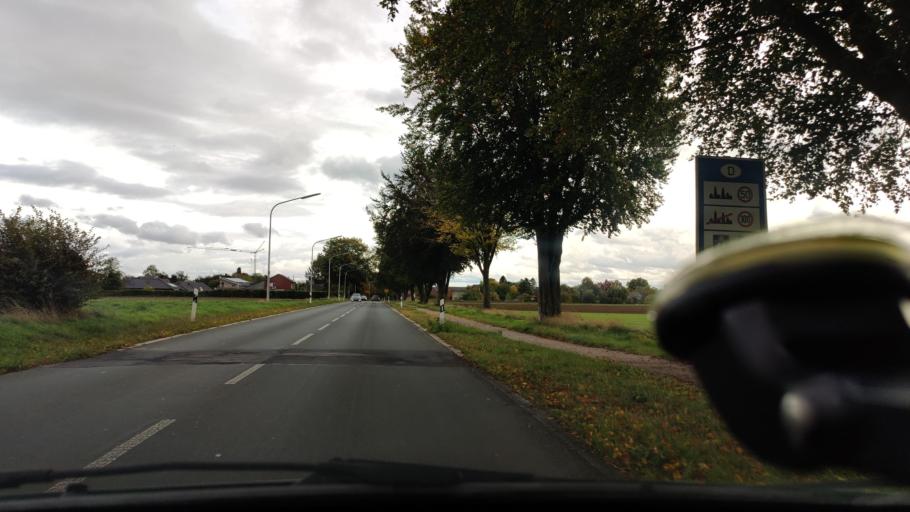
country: NL
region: Limburg
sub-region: Gemeente Roerdalen
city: Posterholt
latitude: 51.1128
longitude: 6.0586
